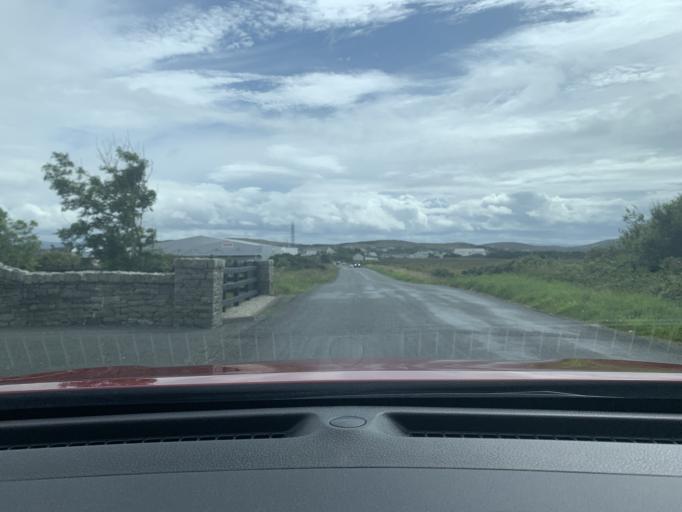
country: IE
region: Ulster
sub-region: County Donegal
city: Dungloe
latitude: 54.9603
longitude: -8.3656
